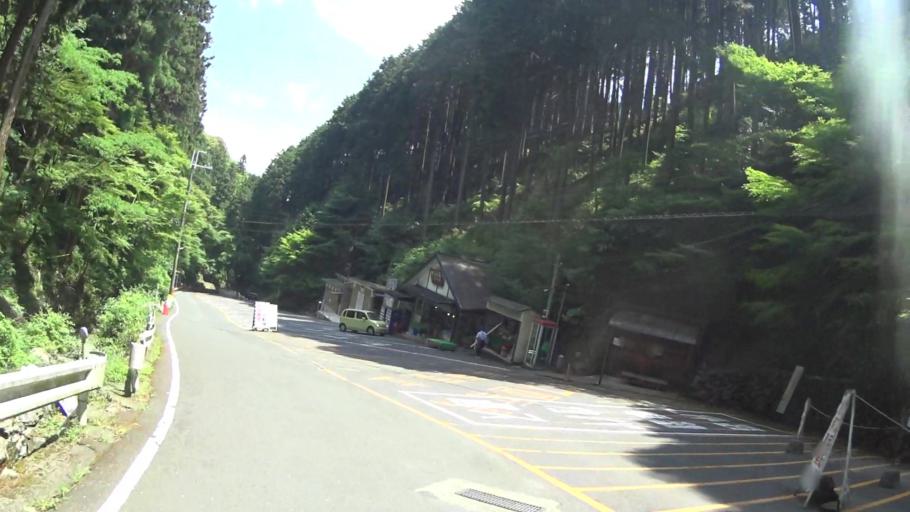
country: JP
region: Kyoto
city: Muko
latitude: 34.9371
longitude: 135.6451
